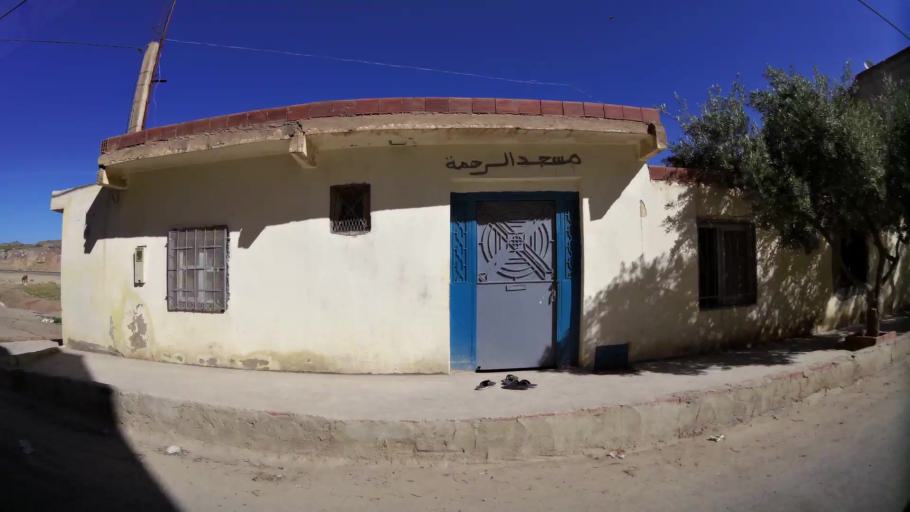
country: MA
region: Oriental
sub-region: Oujda-Angad
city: Oujda
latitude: 34.6467
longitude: -1.9483
